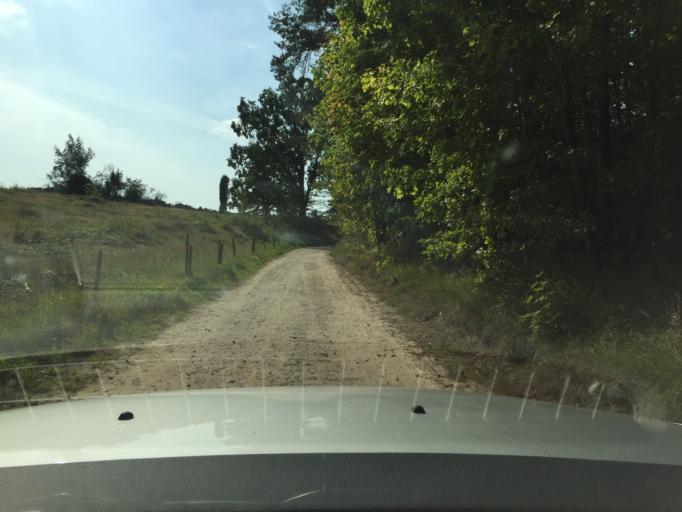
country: SE
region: Skane
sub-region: Kristianstads Kommun
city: Degeberga
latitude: 55.7271
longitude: 14.1142
